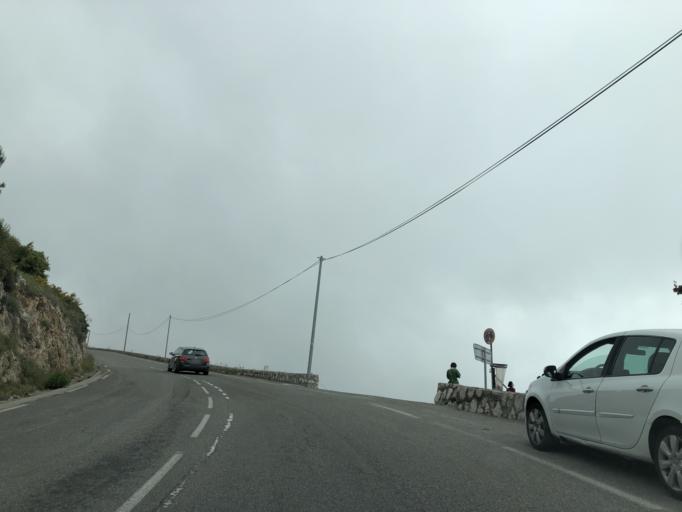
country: FR
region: Provence-Alpes-Cote d'Azur
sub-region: Departement des Alpes-Maritimes
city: Beaulieu-sur-Mer
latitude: 43.7197
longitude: 7.3312
